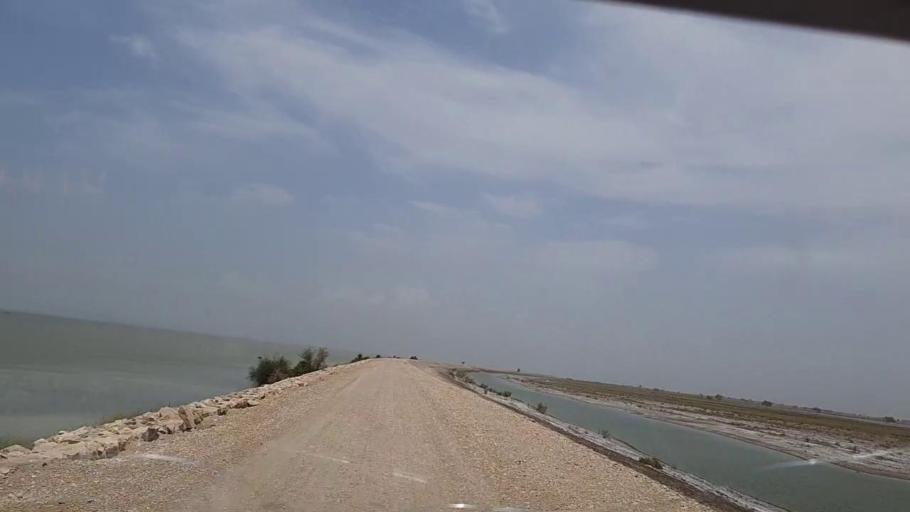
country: PK
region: Sindh
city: Sehwan
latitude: 26.4203
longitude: 67.7289
